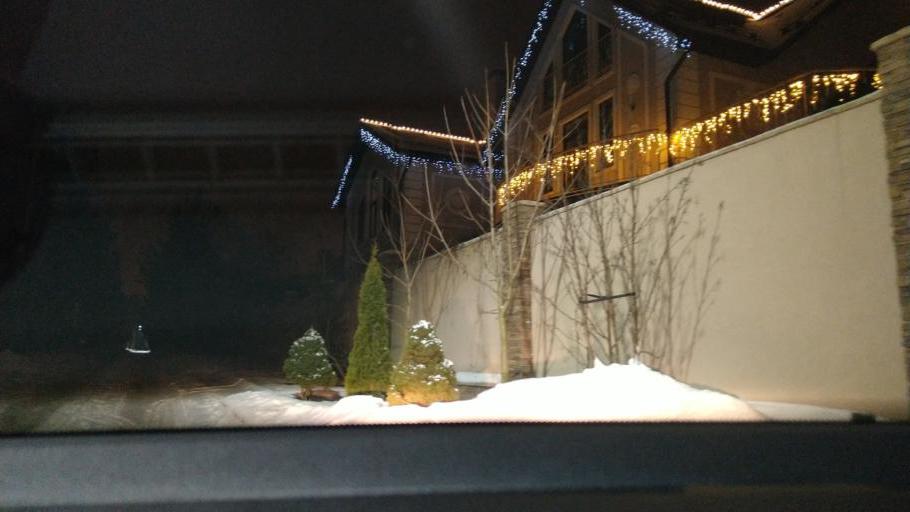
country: RU
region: Moskovskaya
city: Barvikha
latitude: 55.7143
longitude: 37.2868
